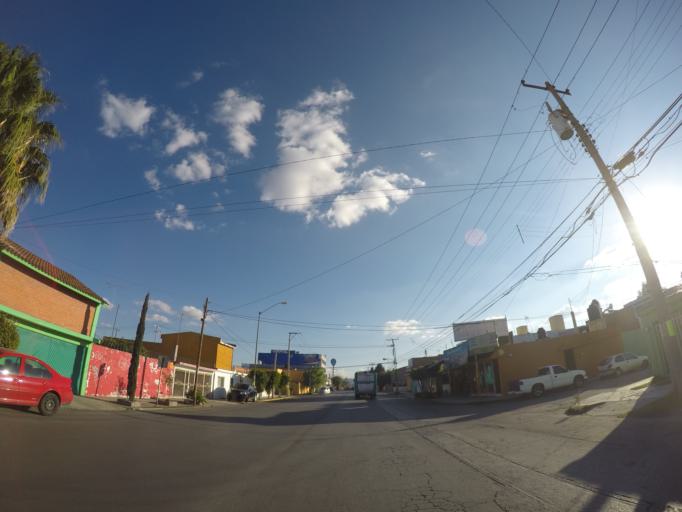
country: MX
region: San Luis Potosi
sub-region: San Luis Potosi
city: San Luis Potosi
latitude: 22.1752
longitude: -100.9982
